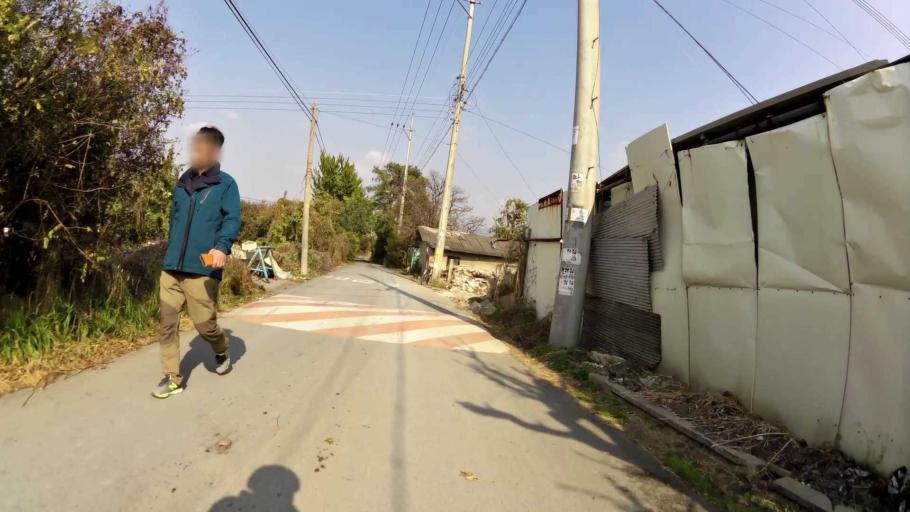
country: KR
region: Gyeongsangbuk-do
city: Gyeongsan-si
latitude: 35.8561
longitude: 128.7098
